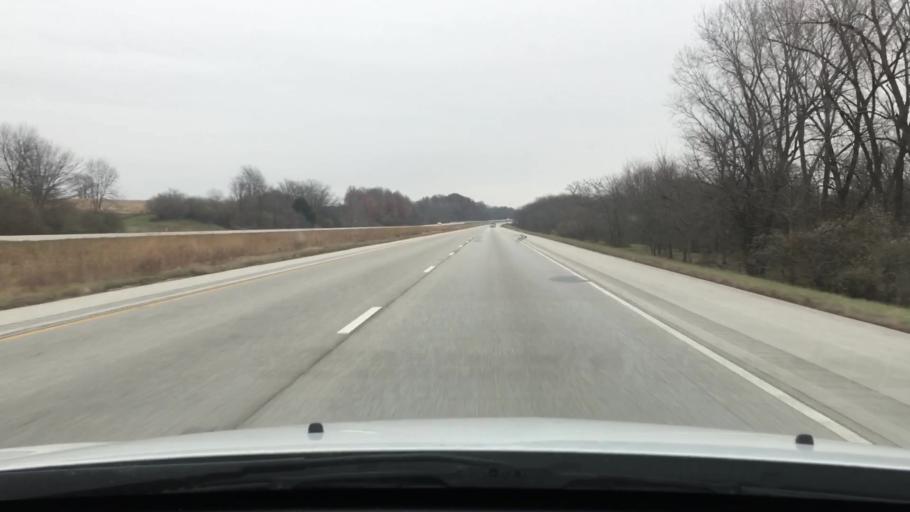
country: US
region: Illinois
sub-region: Scott County
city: Winchester
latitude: 39.6812
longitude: -90.4035
